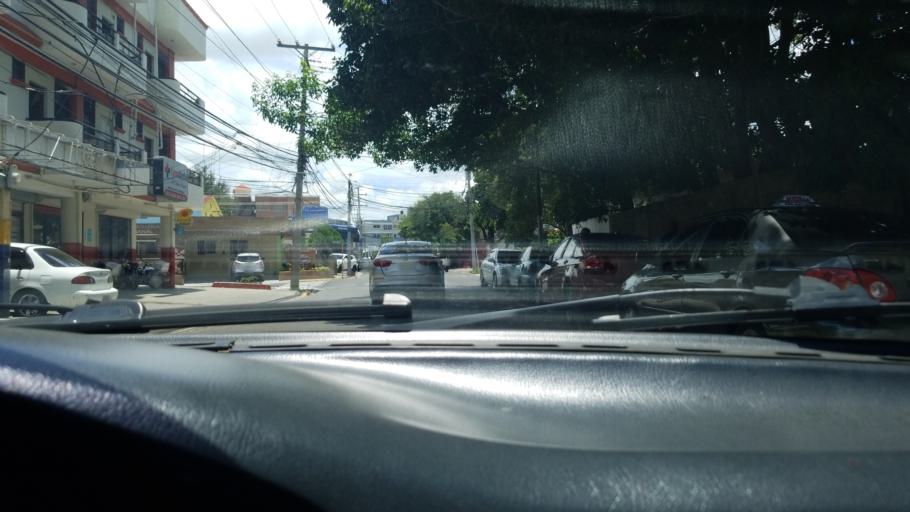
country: DO
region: Santiago
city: Santiago de los Caballeros
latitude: 19.4738
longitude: -70.6869
